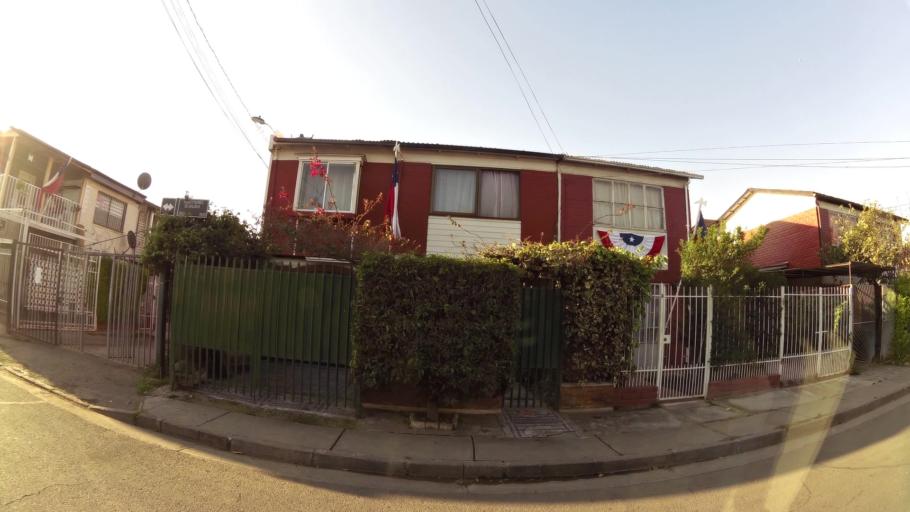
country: CL
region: Santiago Metropolitan
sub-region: Provincia de Santiago
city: La Pintana
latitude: -33.5488
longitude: -70.6204
